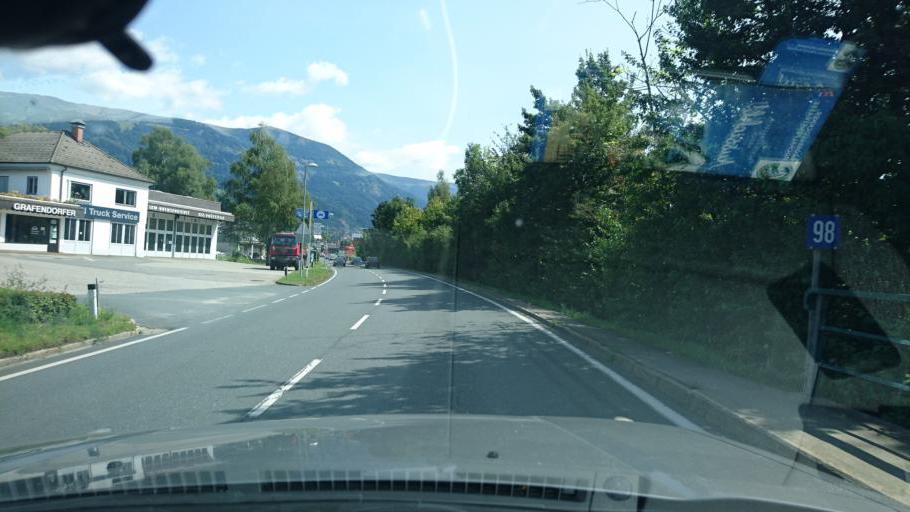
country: AT
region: Carinthia
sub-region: Politischer Bezirk Spittal an der Drau
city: Seeboden
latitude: 46.8153
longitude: 13.5048
